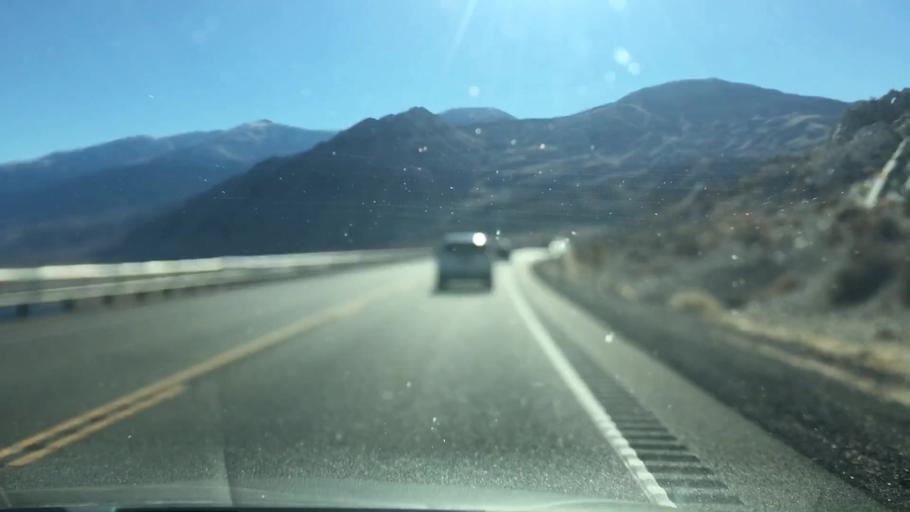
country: US
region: Nevada
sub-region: Mineral County
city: Hawthorne
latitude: 38.7063
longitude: -118.7650
